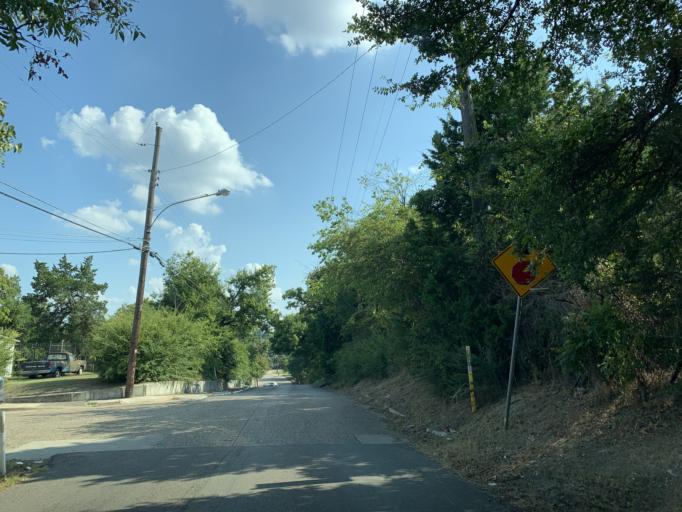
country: US
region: Texas
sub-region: Dallas County
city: Dallas
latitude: 32.7491
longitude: -96.8040
